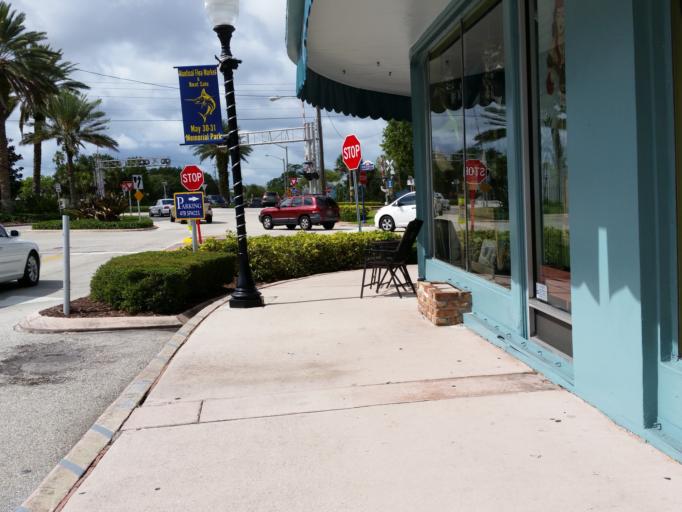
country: US
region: Florida
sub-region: Martin County
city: Stuart
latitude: 27.1983
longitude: -80.2529
